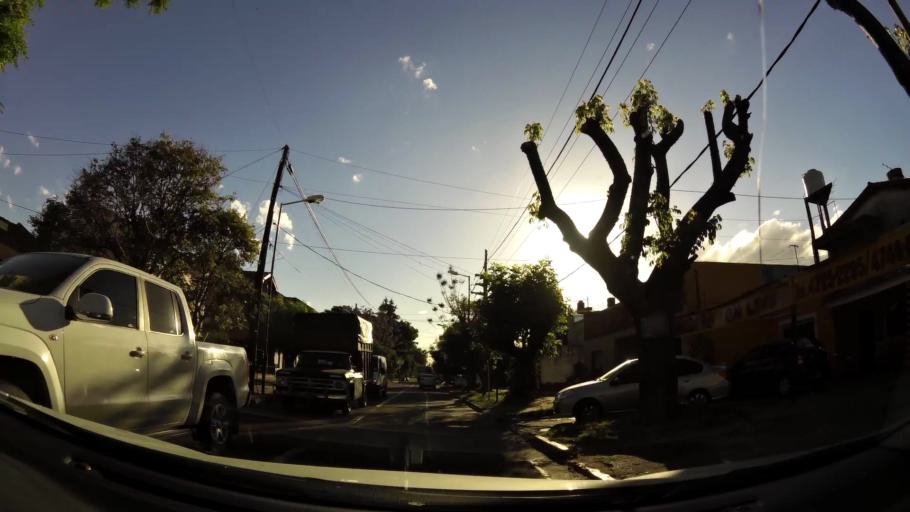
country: AR
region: Buenos Aires
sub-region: Partido de Tigre
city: Tigre
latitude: -34.4620
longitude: -58.5624
